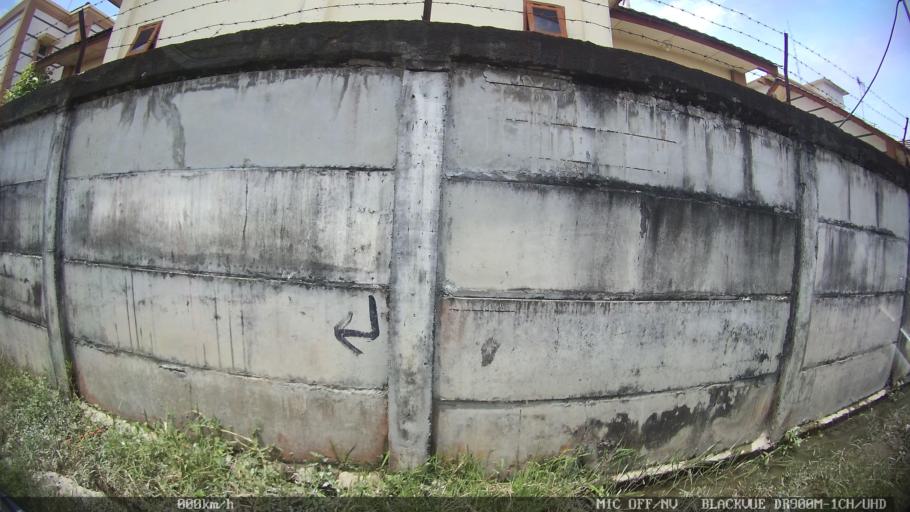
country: ID
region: North Sumatra
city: Percut
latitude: 3.5500
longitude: 98.8539
